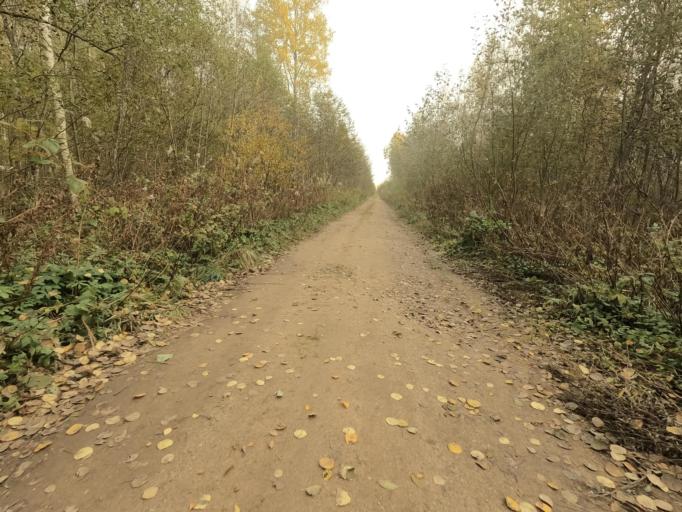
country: RU
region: Novgorod
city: Batetskiy
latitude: 58.8796
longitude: 30.7893
